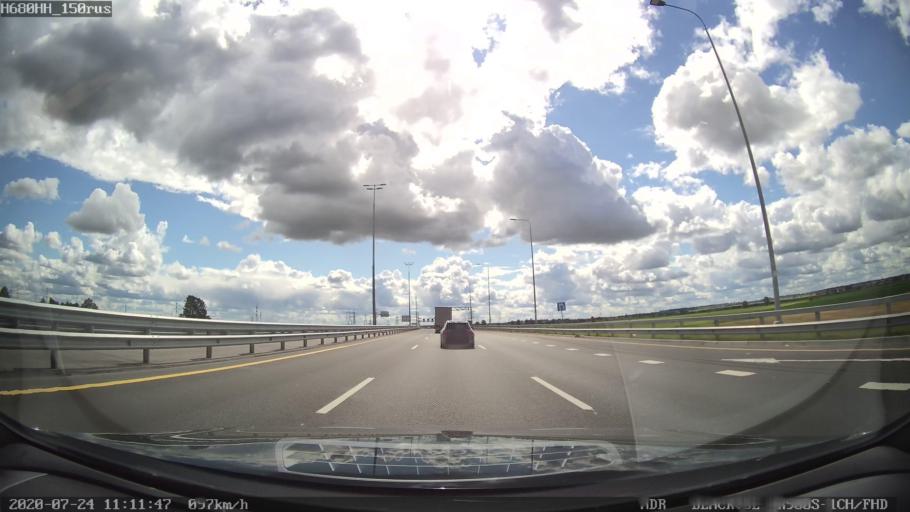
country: RU
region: Leningrad
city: Fedorovskoye
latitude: 59.7180
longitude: 30.5216
